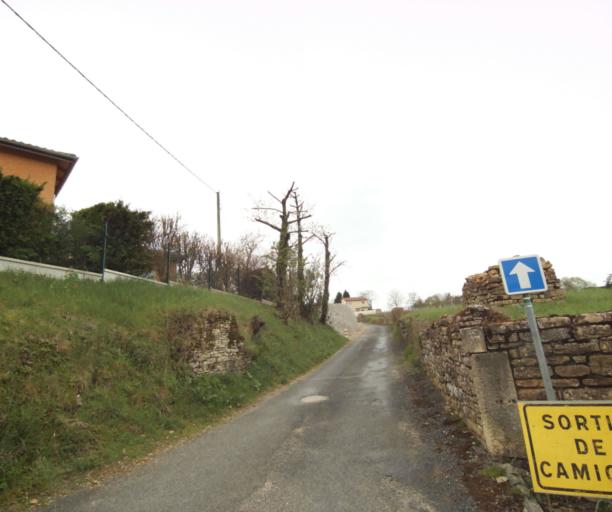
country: FR
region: Bourgogne
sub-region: Departement de Saone-et-Loire
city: Charnay-les-Macon
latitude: 46.3167
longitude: 4.7902
